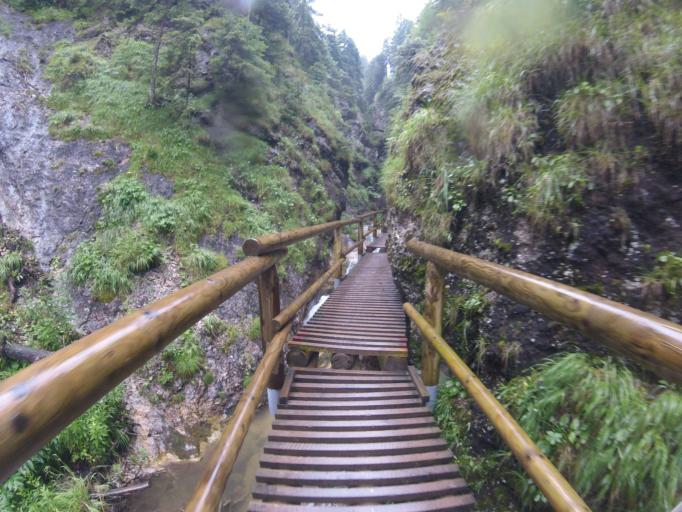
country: SK
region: Zilinsky
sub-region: Okres Zilina
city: Terchova
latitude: 49.2501
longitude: 19.0733
